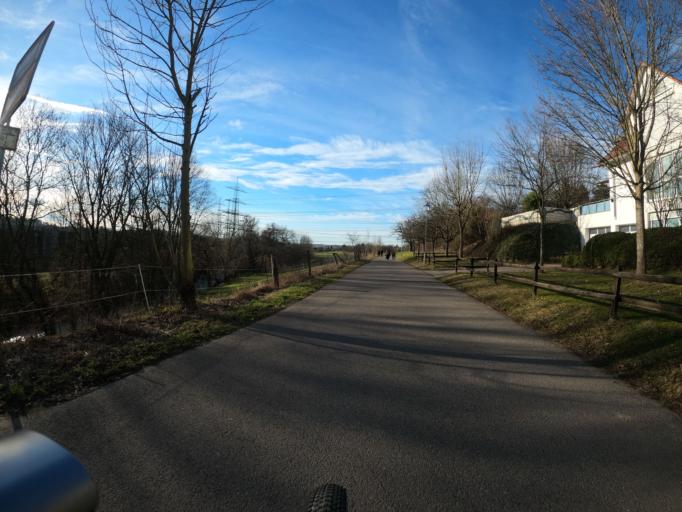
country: DE
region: Baden-Wuerttemberg
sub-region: Regierungsbezirk Stuttgart
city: Wernau
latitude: 48.6676
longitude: 9.4082
